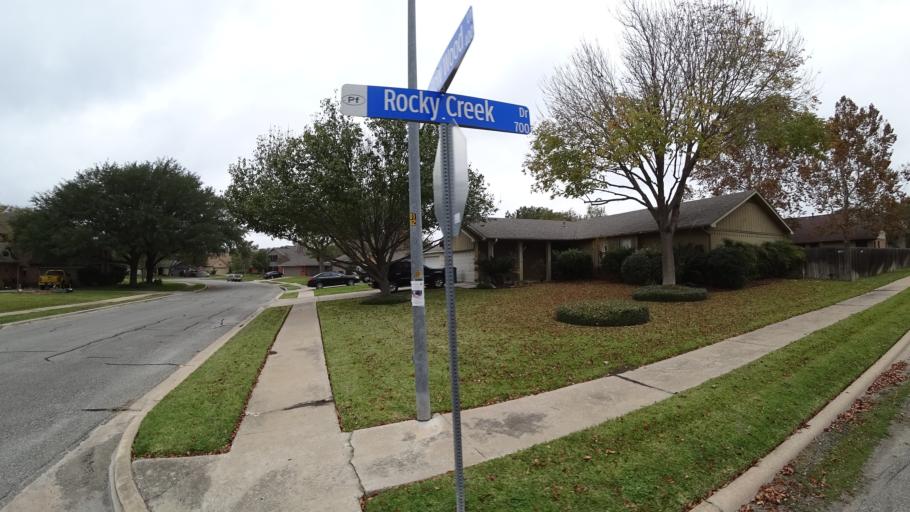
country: US
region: Texas
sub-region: Travis County
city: Pflugerville
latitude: 30.4434
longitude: -97.6154
